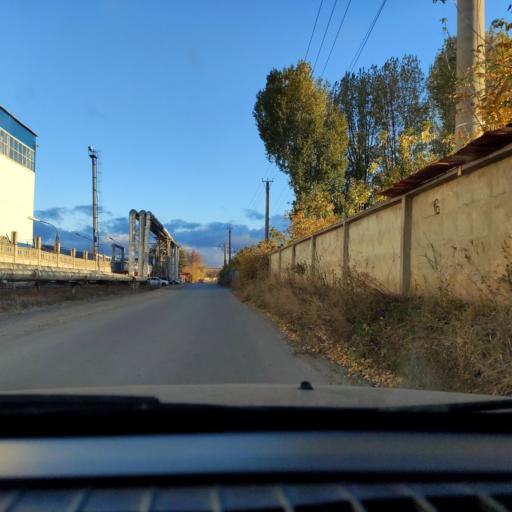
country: RU
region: Samara
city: Tol'yatti
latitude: 53.5777
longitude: 49.2632
